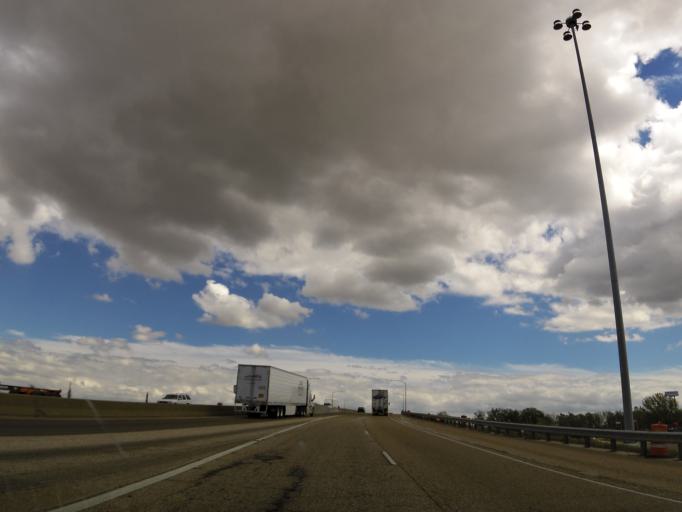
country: US
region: Arkansas
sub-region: Crittenden County
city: West Memphis
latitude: 35.1694
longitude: -90.1878
